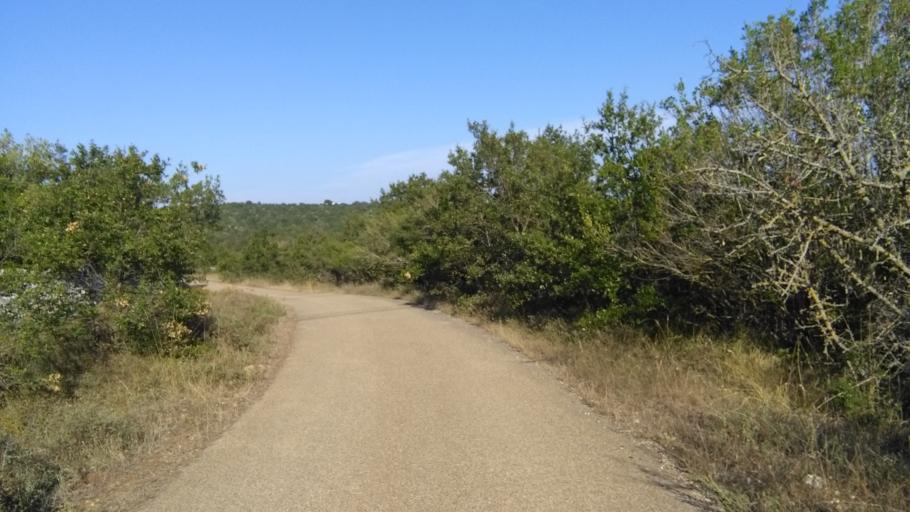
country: IT
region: Apulia
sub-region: Provincia di Bari
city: Putignano
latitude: 40.8178
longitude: 17.0567
